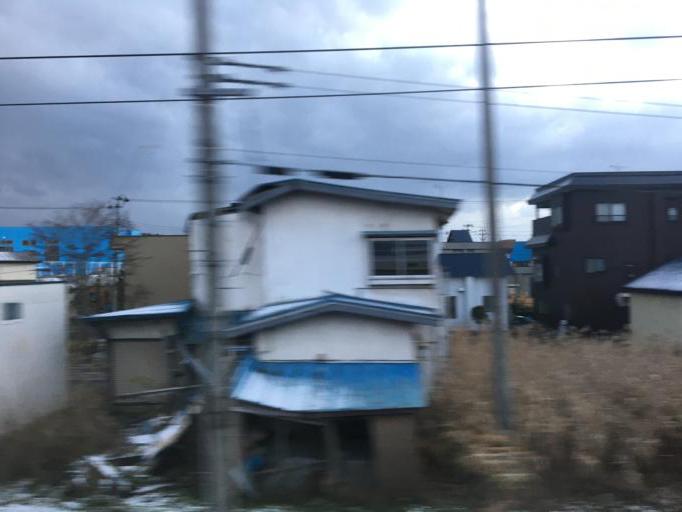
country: JP
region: Aomori
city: Aomori Shi
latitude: 40.8284
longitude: 140.6795
